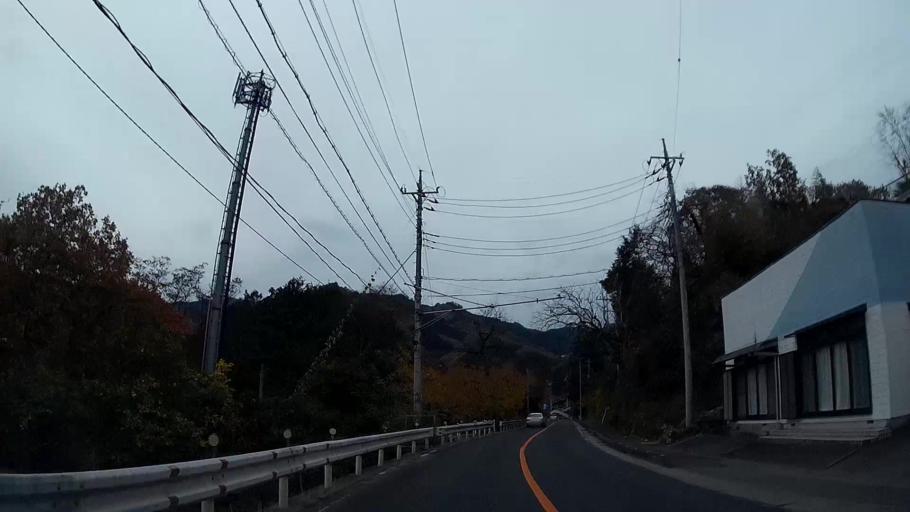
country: JP
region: Saitama
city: Chichibu
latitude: 35.9636
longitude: 138.9844
